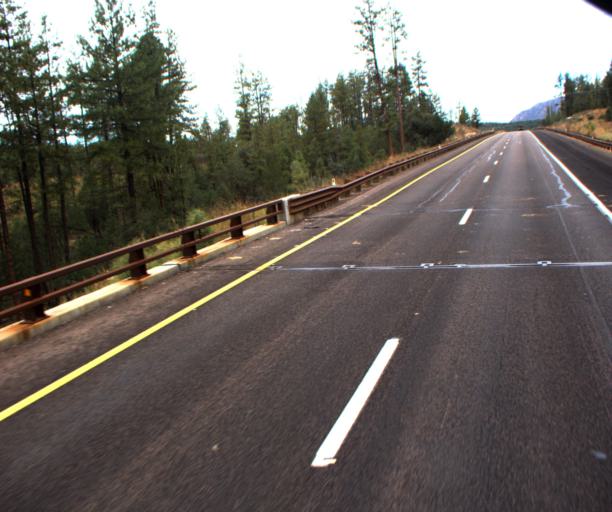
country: US
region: Arizona
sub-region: Gila County
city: Star Valley
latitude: 34.3106
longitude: -111.1102
